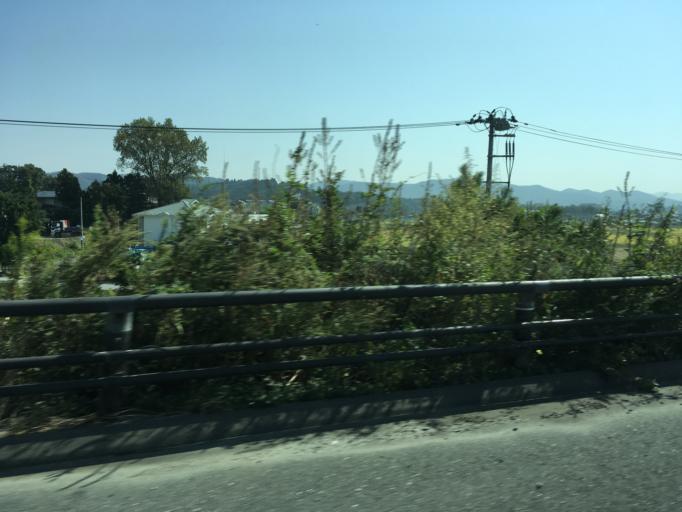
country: JP
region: Miyagi
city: Wakuya
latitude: 38.6649
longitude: 141.2656
